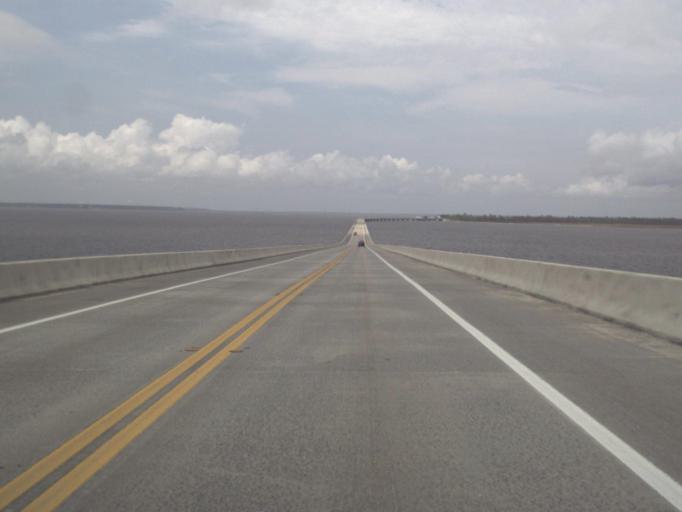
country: US
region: Florida
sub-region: Santa Rosa County
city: Oriole Beach
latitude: 30.4193
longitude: -87.0897
